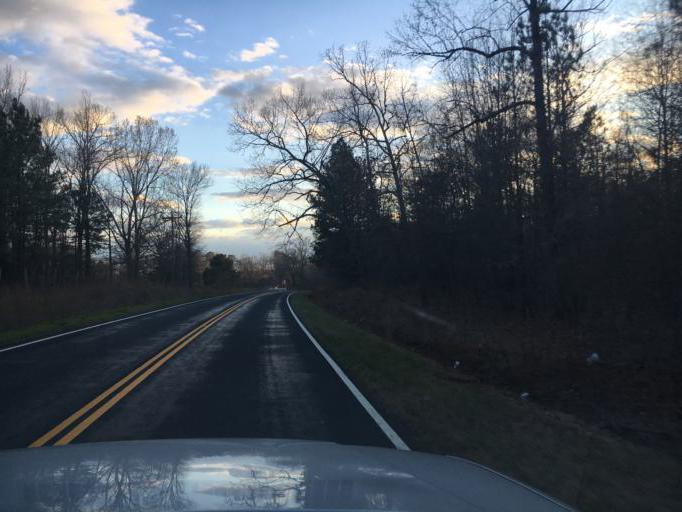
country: US
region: South Carolina
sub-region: Greenwood County
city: Greenwood
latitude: 34.0942
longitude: -82.1897
